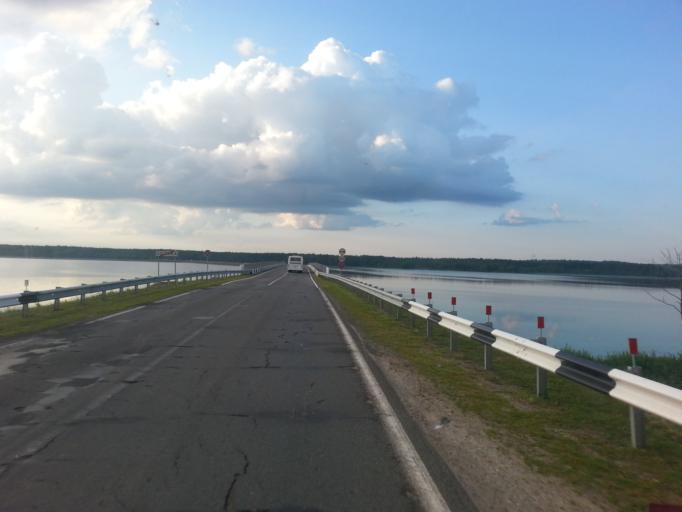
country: BY
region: Minsk
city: Il'ya
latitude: 54.5078
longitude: 27.2245
